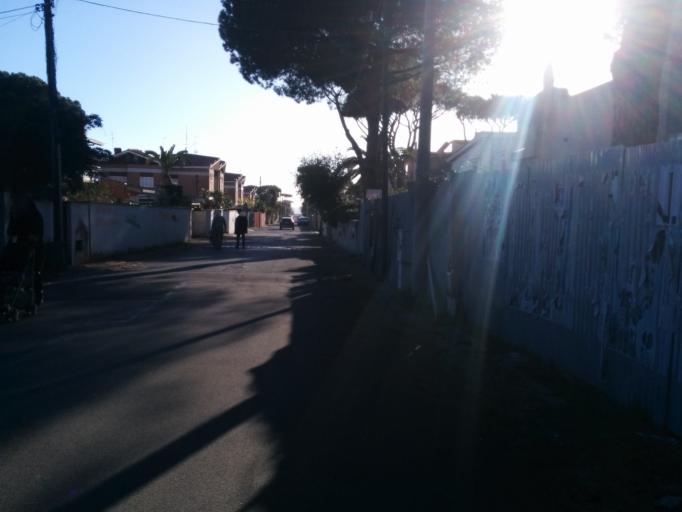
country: IT
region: Latium
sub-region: Citta metropolitana di Roma Capitale
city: Lavinio
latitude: 41.4991
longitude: 12.5934
